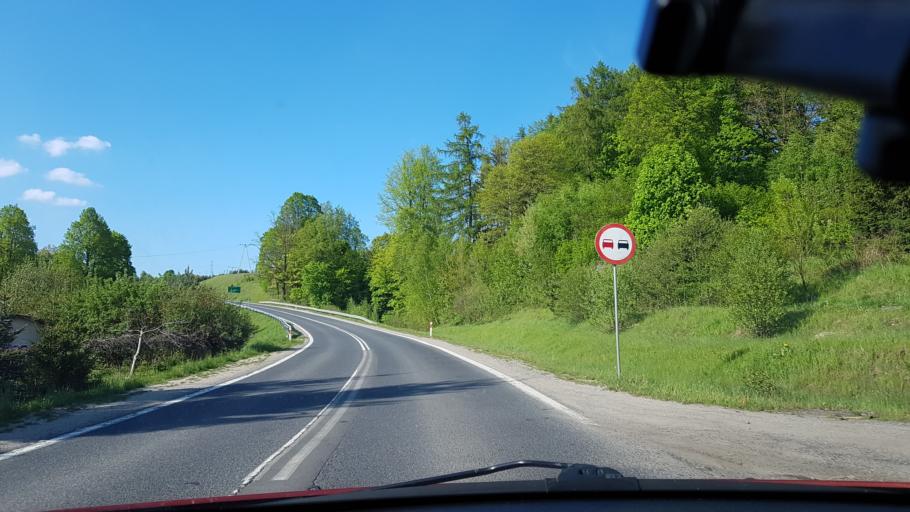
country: PL
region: Lower Silesian Voivodeship
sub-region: Powiat klodzki
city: Nowa Ruda
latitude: 50.5787
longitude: 16.5260
